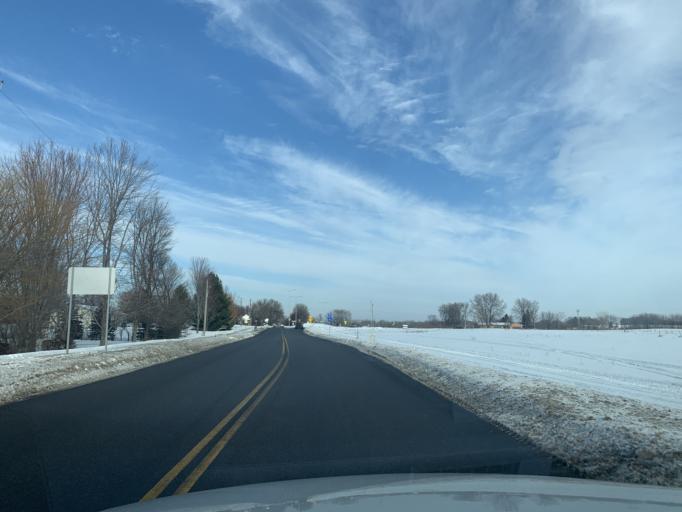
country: US
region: Minnesota
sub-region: Wright County
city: Albertville
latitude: 45.2220
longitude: -93.6441
